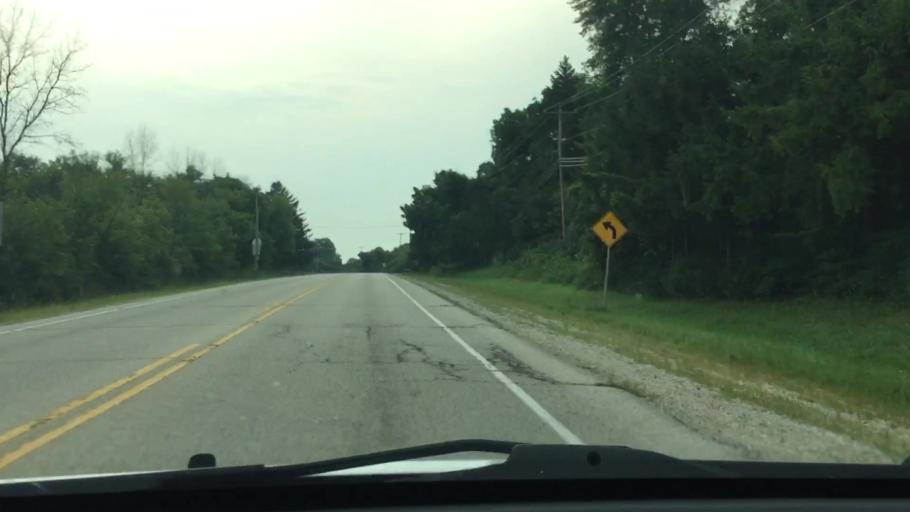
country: US
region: Wisconsin
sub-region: Waukesha County
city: New Berlin
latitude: 42.9908
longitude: -88.1438
